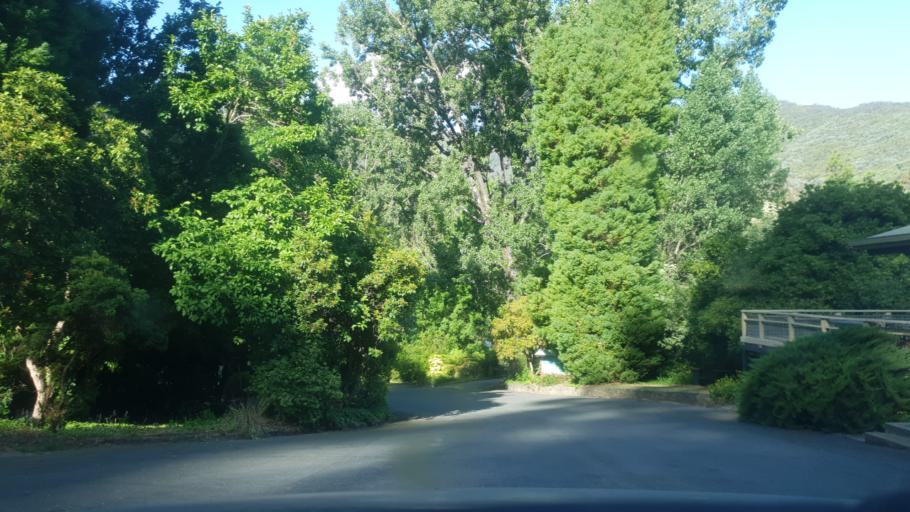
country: AU
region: Victoria
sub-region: Alpine
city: Mount Beauty
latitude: -36.8029
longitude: 147.2240
